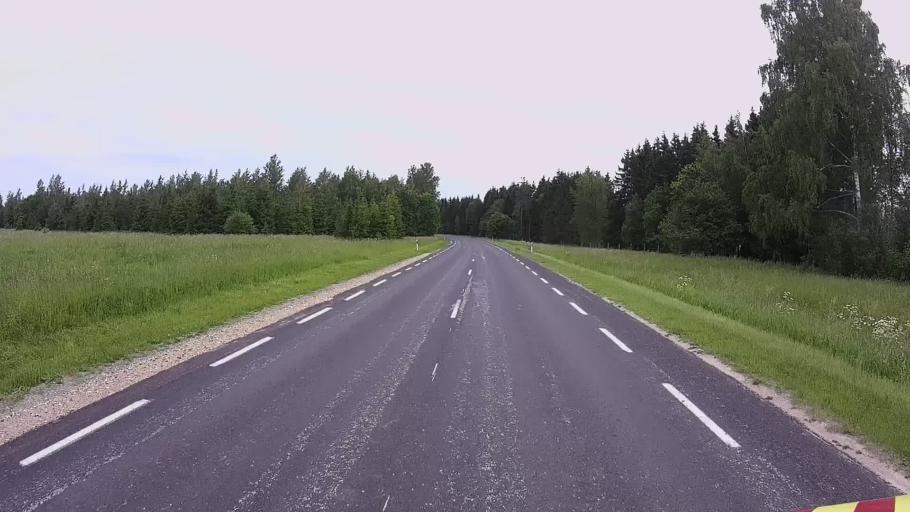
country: EE
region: Viljandimaa
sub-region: Karksi vald
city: Karksi-Nuia
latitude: 58.2022
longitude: 25.6190
